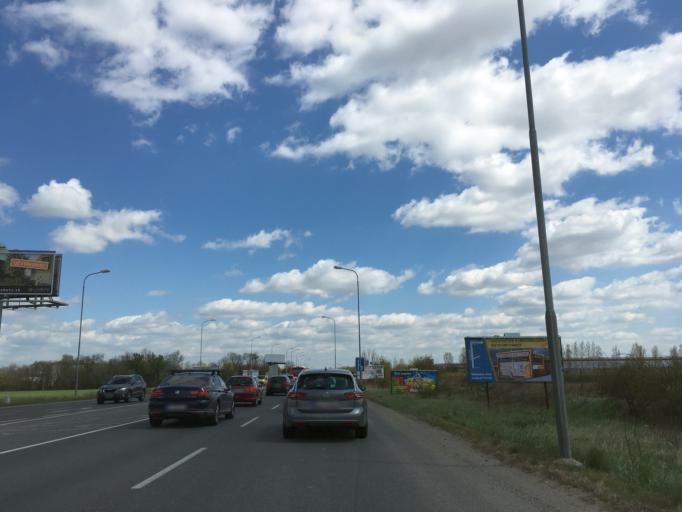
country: SK
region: Bratislavsky
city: Svaty Jur
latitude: 48.1914
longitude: 17.2201
